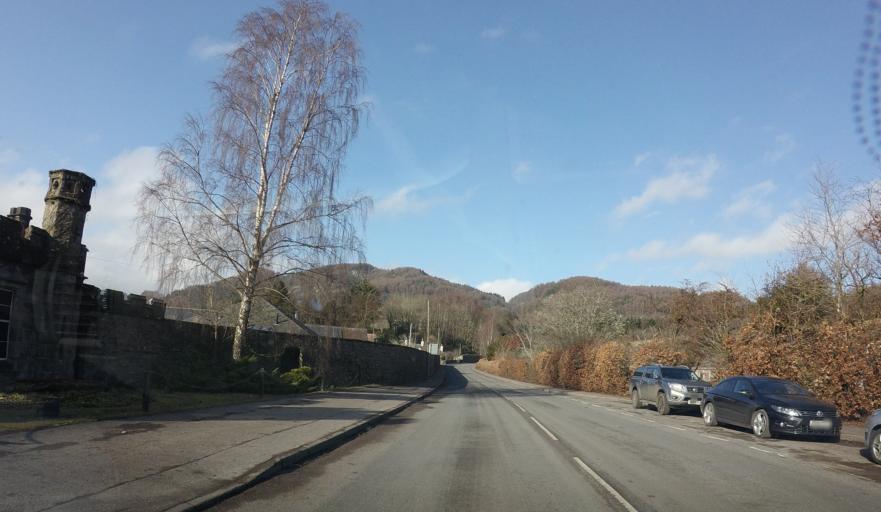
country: GB
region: Scotland
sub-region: Perth and Kinross
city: Bankfoot
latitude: 56.5682
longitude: -3.5868
